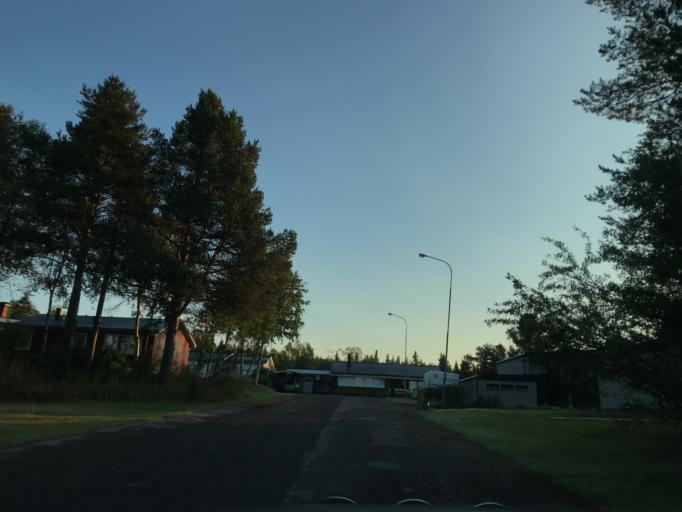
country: SE
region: Norrbotten
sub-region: Gallivare Kommun
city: Malmberget
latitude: 67.6513
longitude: 21.0487
